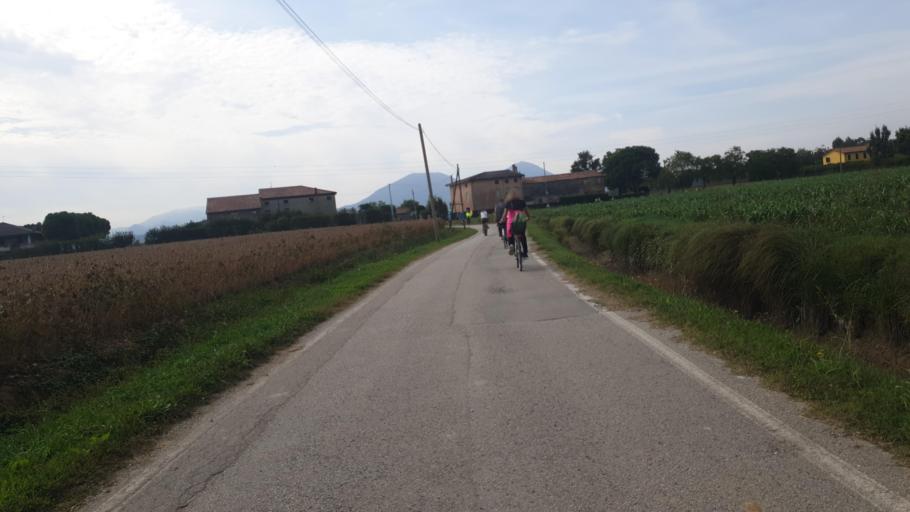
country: IT
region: Veneto
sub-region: Provincia di Padova
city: Cervarese Santa Croce
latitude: 45.4154
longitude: 11.7057
